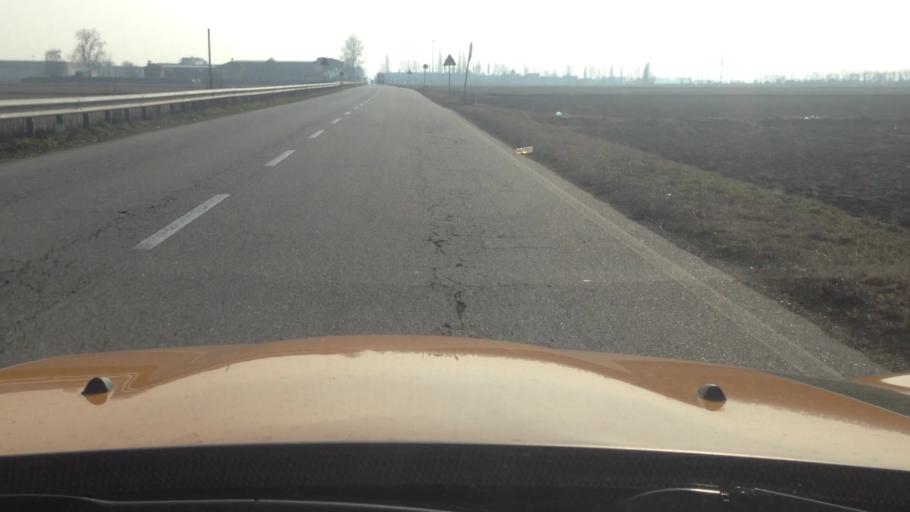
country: IT
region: Piedmont
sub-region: Provincia di Novara
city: San Pietro Mosezzo
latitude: 45.4676
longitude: 8.5579
